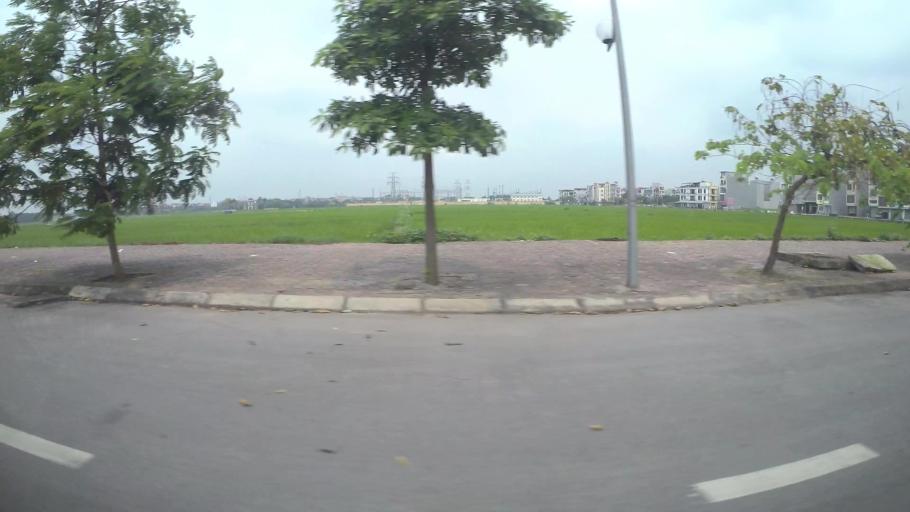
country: VN
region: Ha Noi
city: Trau Quy
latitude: 21.0662
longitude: 105.9118
